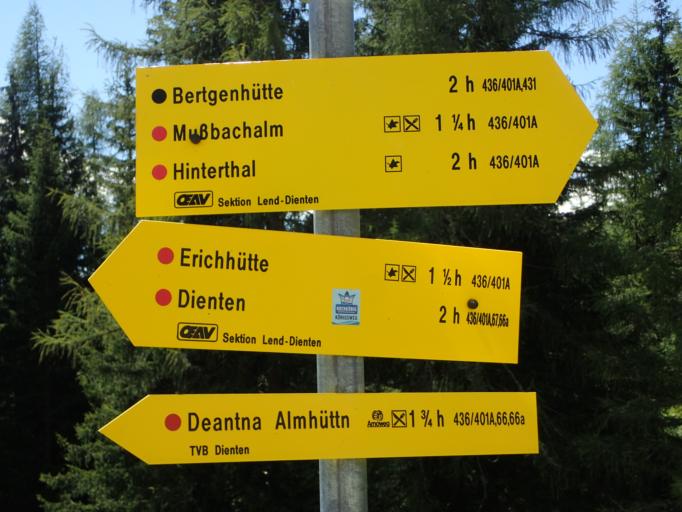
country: AT
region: Salzburg
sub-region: Politischer Bezirk Zell am See
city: Dienten am Hochkonig
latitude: 47.4045
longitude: 13.0137
